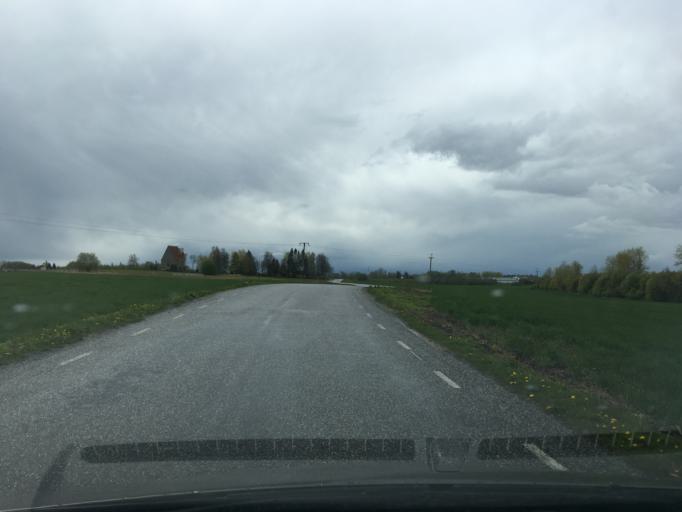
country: EE
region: Harju
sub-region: Joelaehtme vald
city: Loo
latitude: 59.4234
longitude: 24.9865
